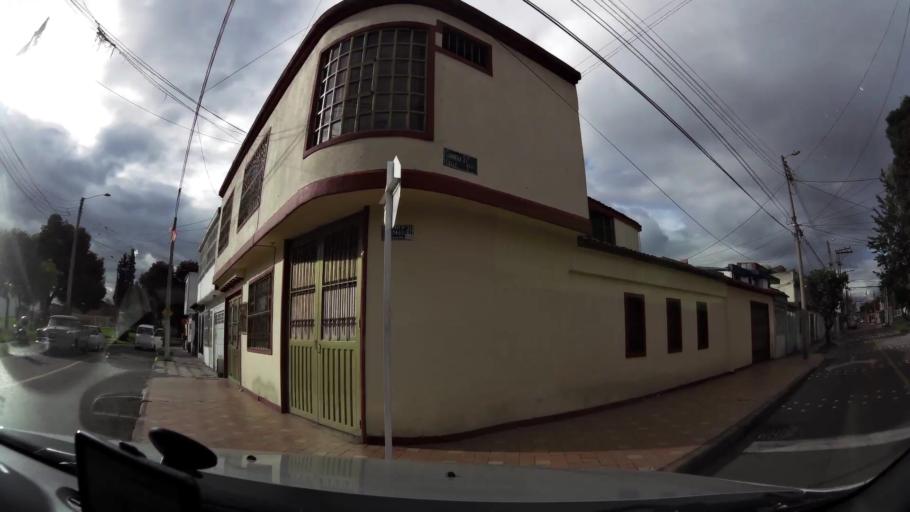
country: CO
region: Bogota D.C.
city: Bogota
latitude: 4.6058
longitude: -74.1107
